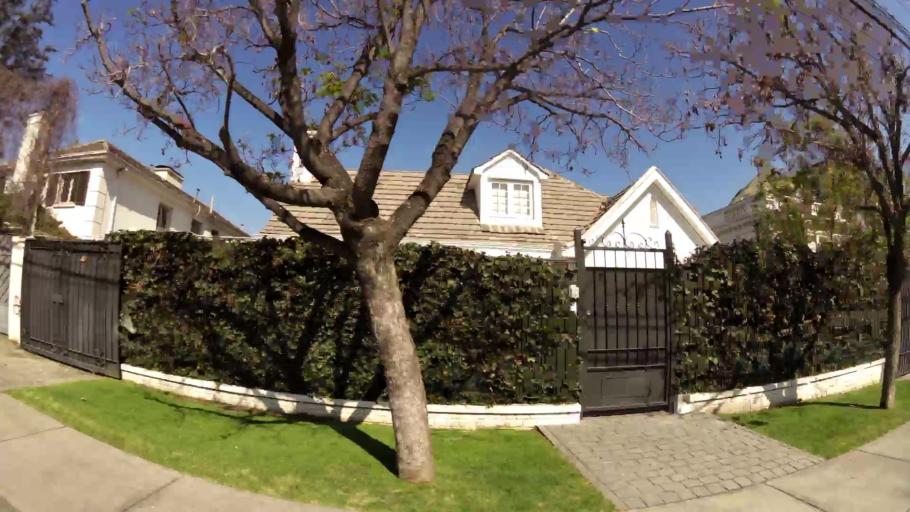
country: CL
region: Santiago Metropolitan
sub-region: Provincia de Santiago
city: Villa Presidente Frei, Nunoa, Santiago, Chile
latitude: -33.4187
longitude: -70.5809
